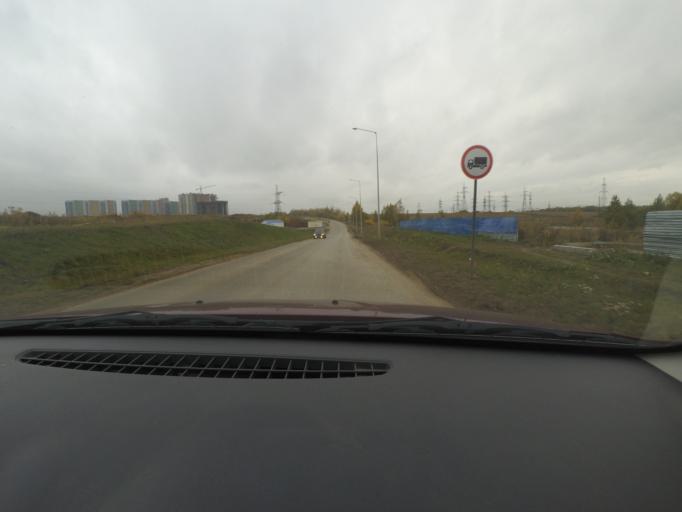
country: RU
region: Nizjnij Novgorod
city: Afonino
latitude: 56.2442
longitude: 44.0593
